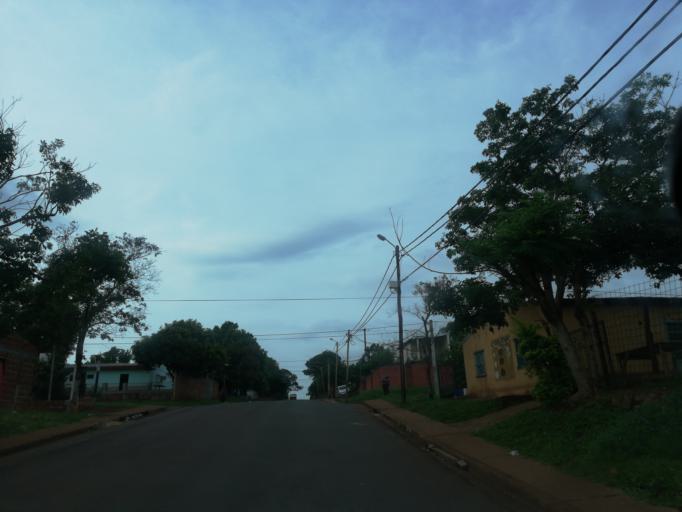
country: AR
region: Misiones
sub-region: Departamento de Capital
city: Posadas
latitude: -27.4331
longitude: -55.9086
